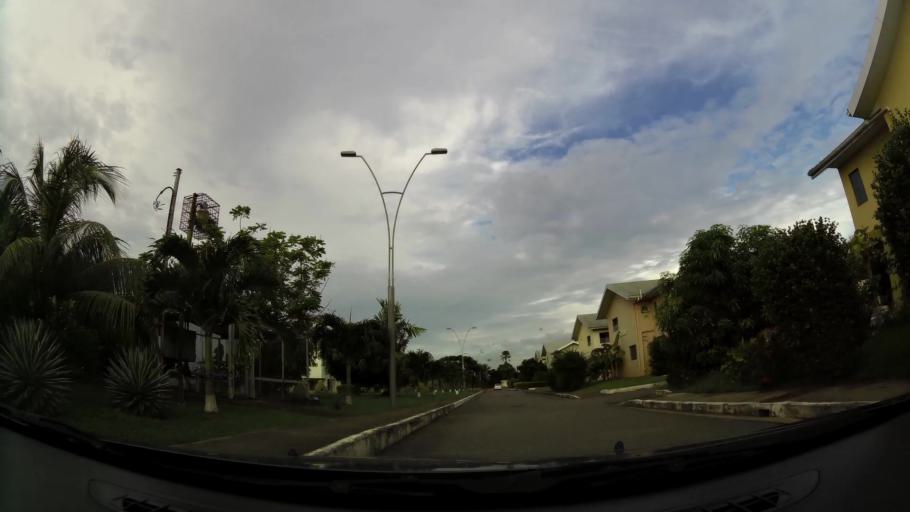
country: TT
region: Tunapuna/Piarco
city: Tunapuna
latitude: 10.6398
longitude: -61.4128
